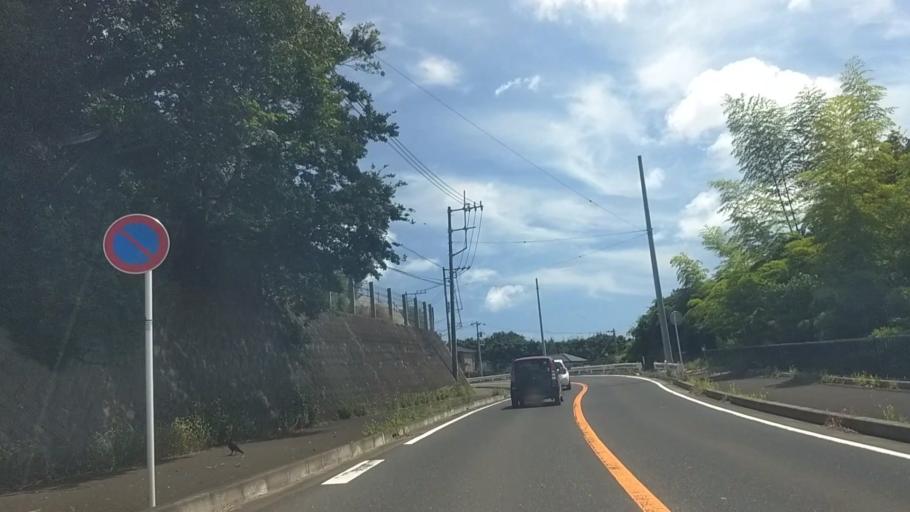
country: JP
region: Kanagawa
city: Miura
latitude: 35.2018
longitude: 139.6500
